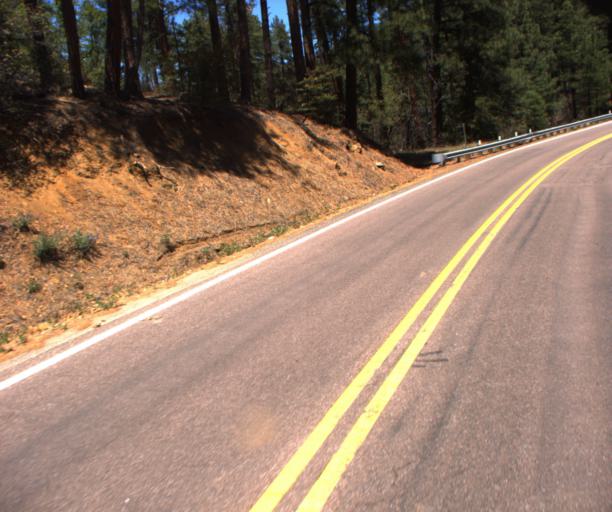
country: US
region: Arizona
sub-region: Yavapai County
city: Prescott
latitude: 34.4837
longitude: -112.5041
